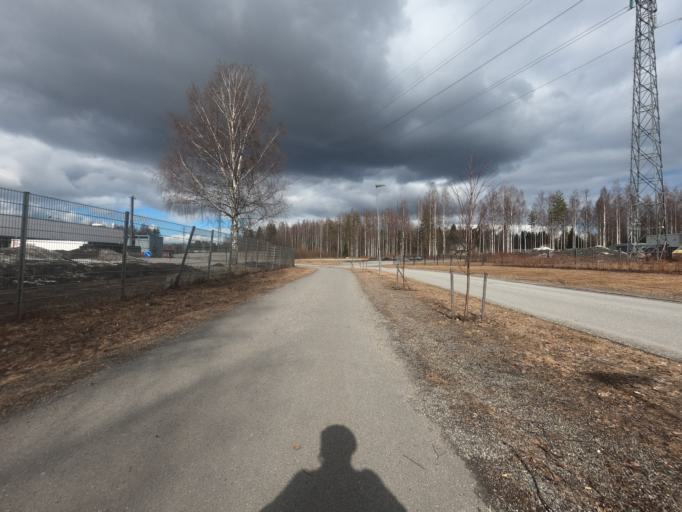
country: FI
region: North Karelia
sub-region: Joensuu
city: Joensuu
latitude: 62.6034
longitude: 29.7860
